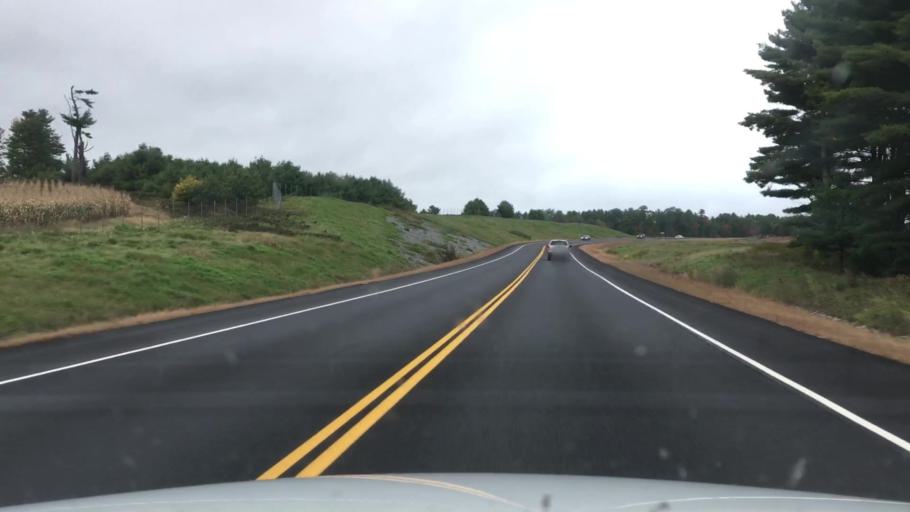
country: US
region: Maine
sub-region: Cumberland County
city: New Gloucester
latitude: 43.8923
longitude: -70.3442
